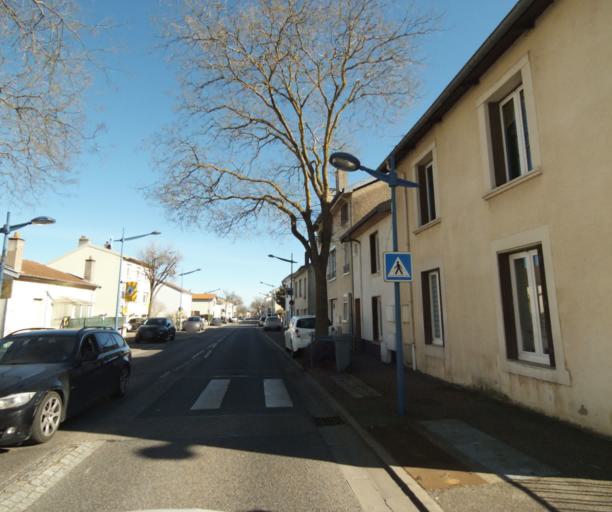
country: FR
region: Lorraine
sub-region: Departement de Meurthe-et-Moselle
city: Vandoeuvre-les-Nancy
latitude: 48.6527
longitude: 6.1881
